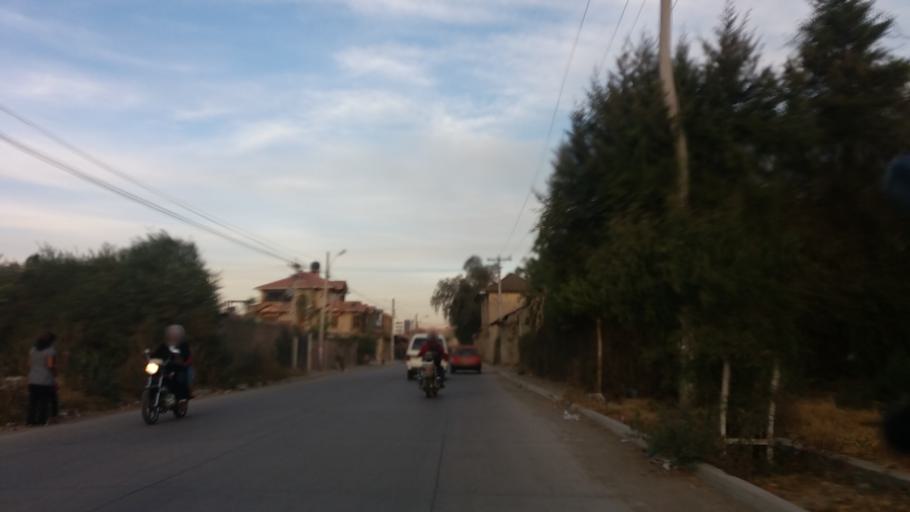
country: BO
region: Cochabamba
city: Cochabamba
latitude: -17.3738
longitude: -66.1996
